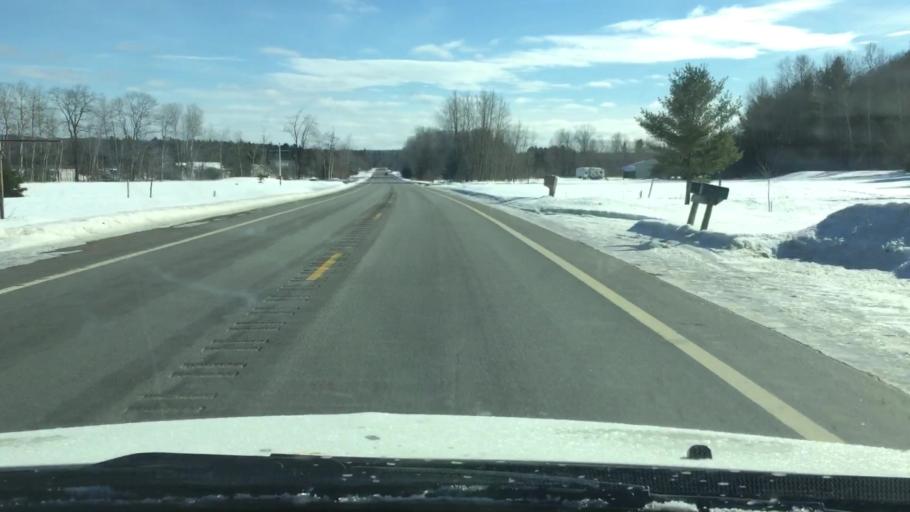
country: US
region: Michigan
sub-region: Charlevoix County
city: East Jordan
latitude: 45.0655
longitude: -85.0826
